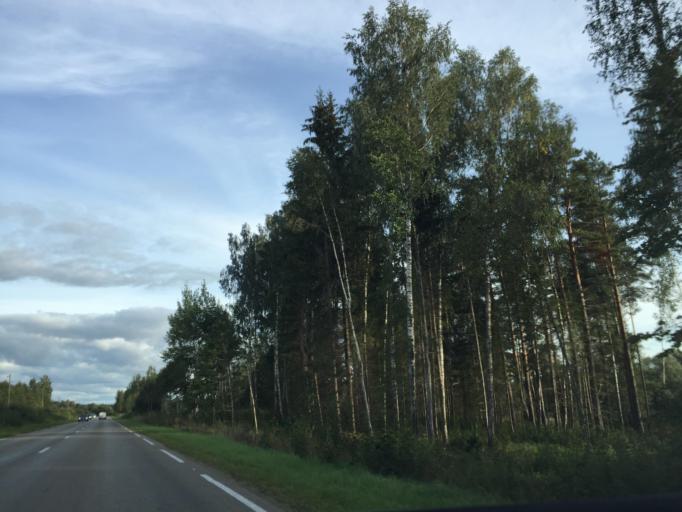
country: LV
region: Jaunjelgava
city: Jaunjelgava
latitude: 56.3560
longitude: 25.0498
